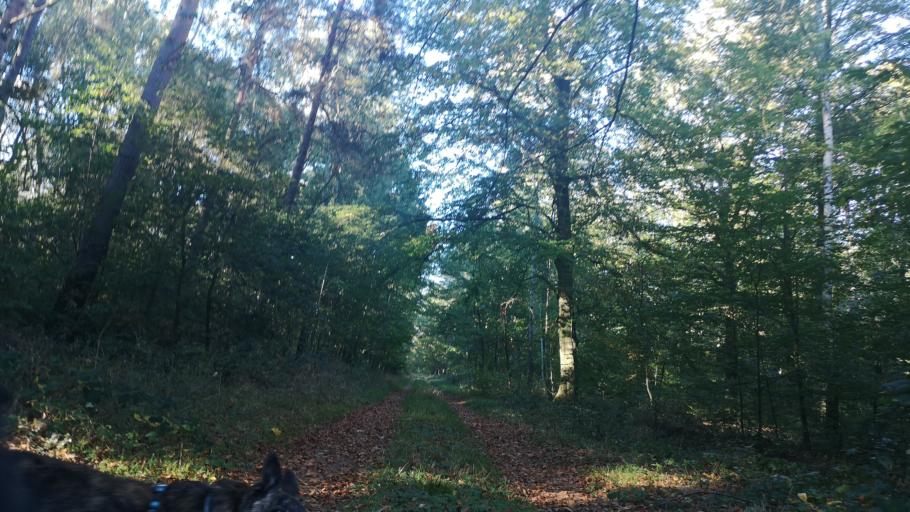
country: DE
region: North Rhine-Westphalia
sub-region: Regierungsbezirk Koln
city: Kreuzau
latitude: 50.7455
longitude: 6.5166
